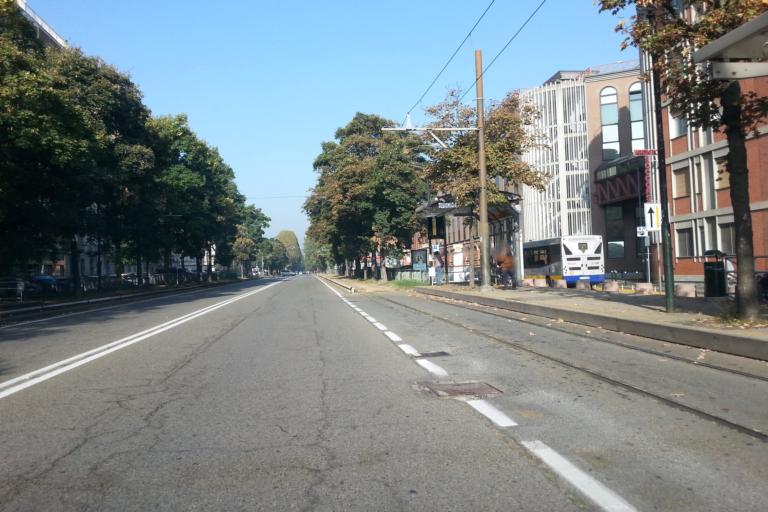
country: IT
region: Piedmont
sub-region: Provincia di Torino
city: Turin
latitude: 45.0693
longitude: 7.7062
